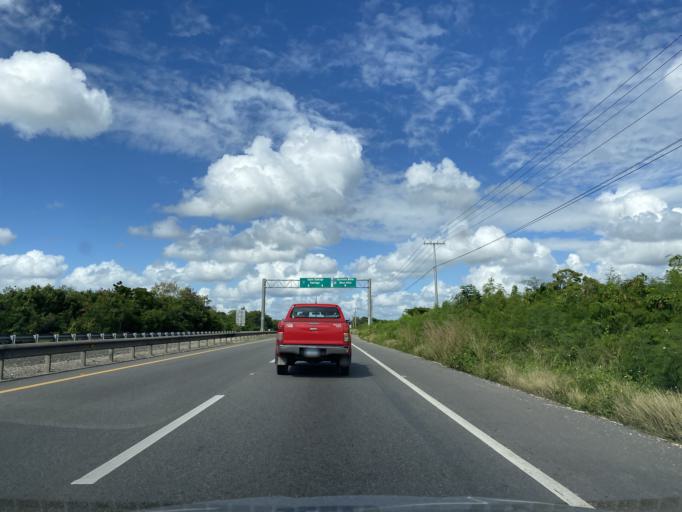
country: DO
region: Santo Domingo
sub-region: Santo Domingo
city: Boca Chica
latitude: 18.4463
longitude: -69.5896
